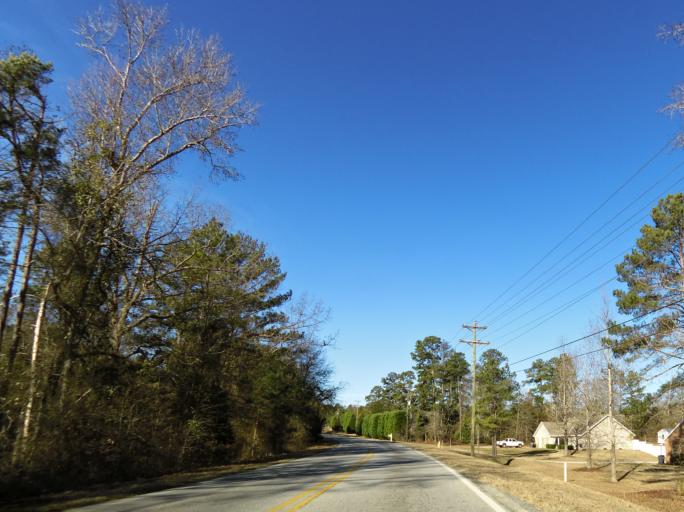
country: US
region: Georgia
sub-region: Bibb County
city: West Point
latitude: 32.7562
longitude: -83.7462
